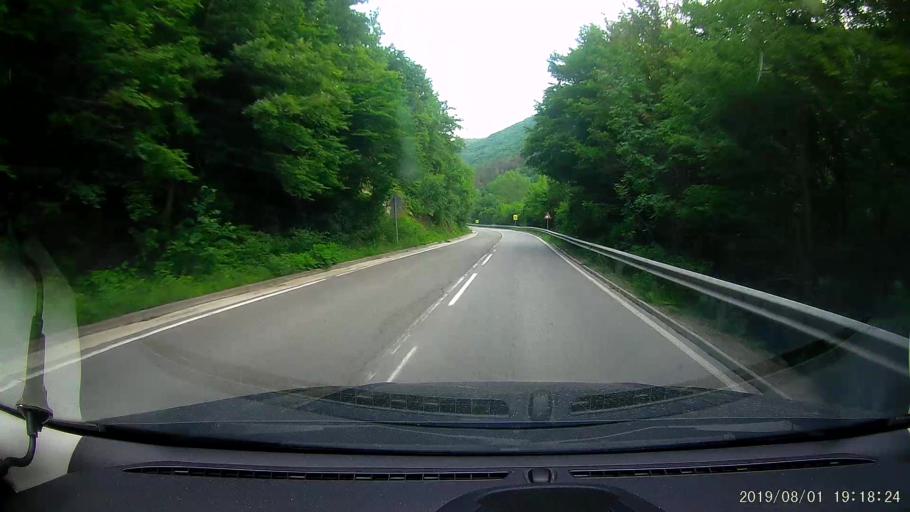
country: BG
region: Shumen
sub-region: Obshtina Smyadovo
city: Smyadovo
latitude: 42.9137
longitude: 26.9405
